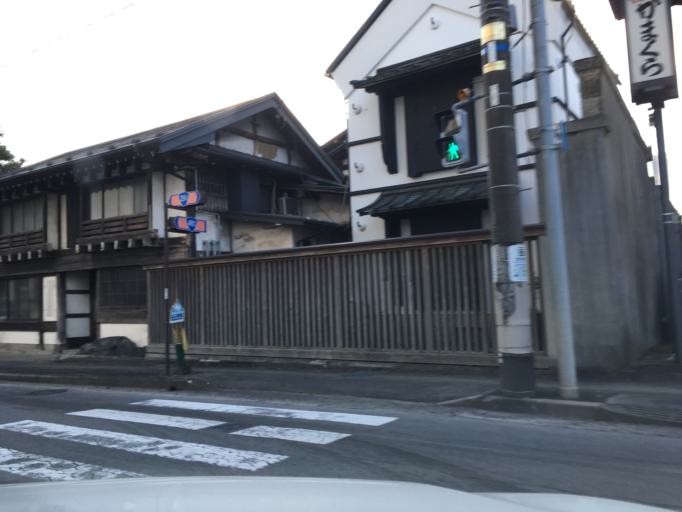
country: JP
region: Tochigi
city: Otawara
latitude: 36.8591
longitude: 140.1171
